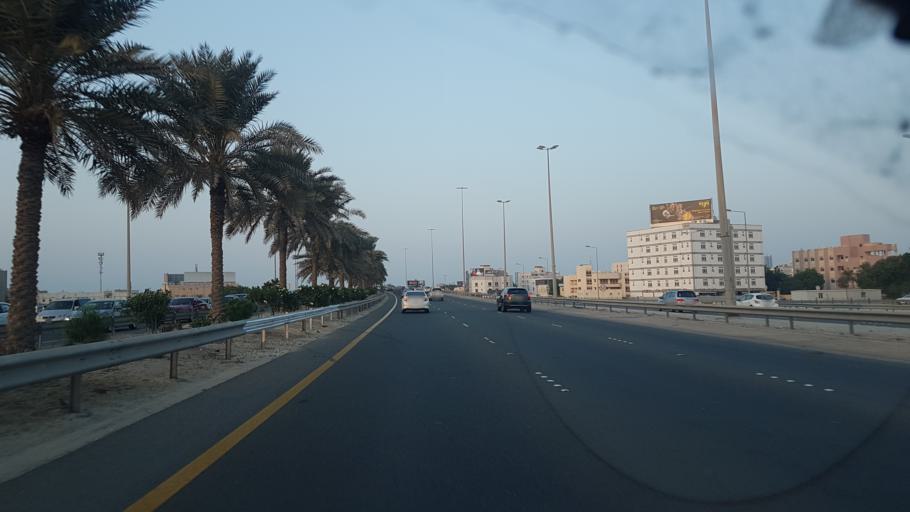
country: BH
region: Manama
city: Jidd Hafs
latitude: 26.2135
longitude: 50.5198
